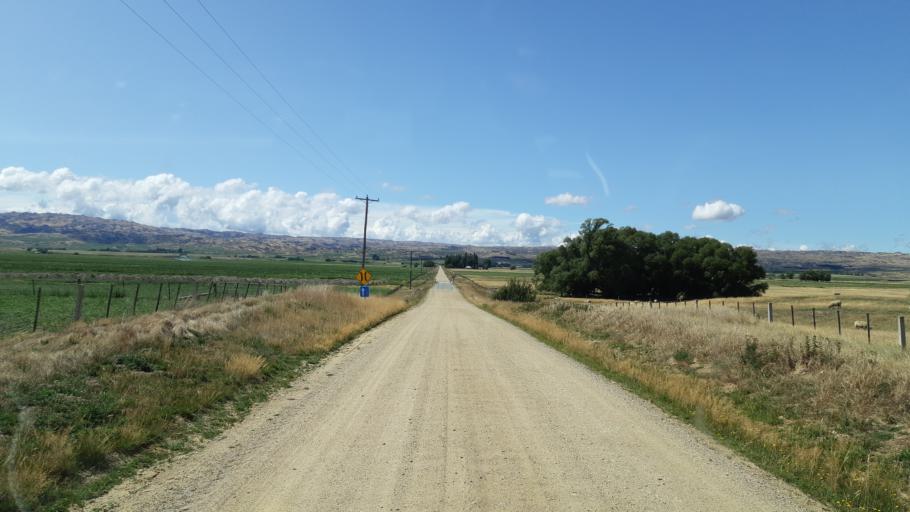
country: NZ
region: Otago
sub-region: Queenstown-Lakes District
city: Wanaka
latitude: -45.2030
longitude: 169.6491
